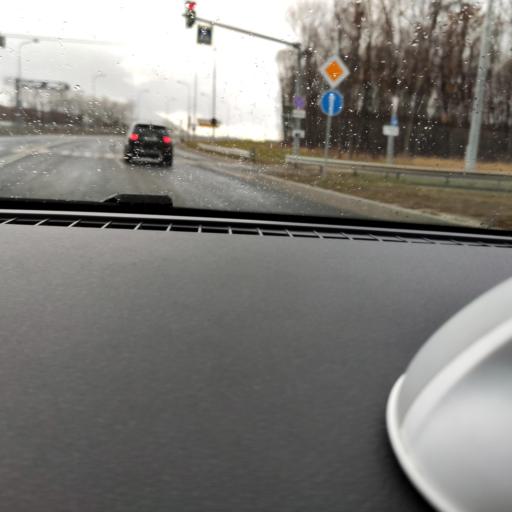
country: RU
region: Samara
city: Petra-Dubrava
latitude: 53.2793
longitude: 50.2534
